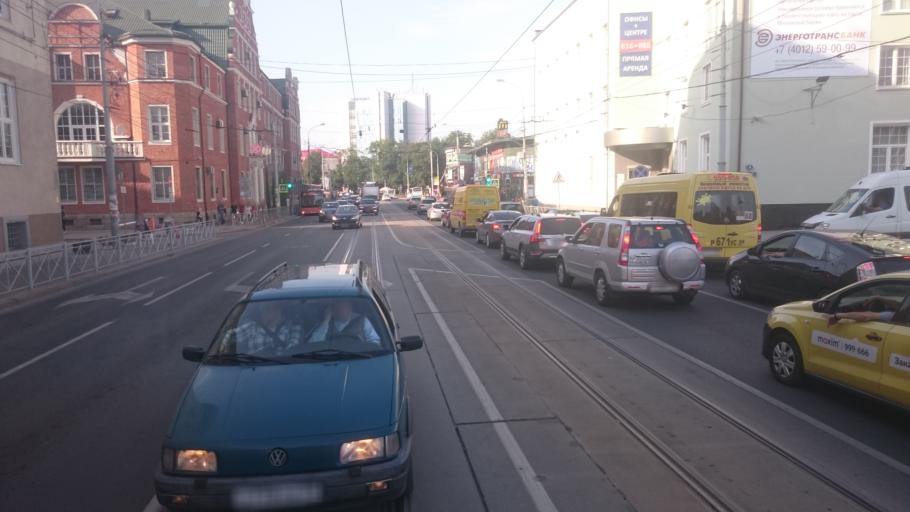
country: RU
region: Kaliningrad
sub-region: Gorod Kaliningrad
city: Kaliningrad
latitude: 54.7209
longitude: 20.4987
